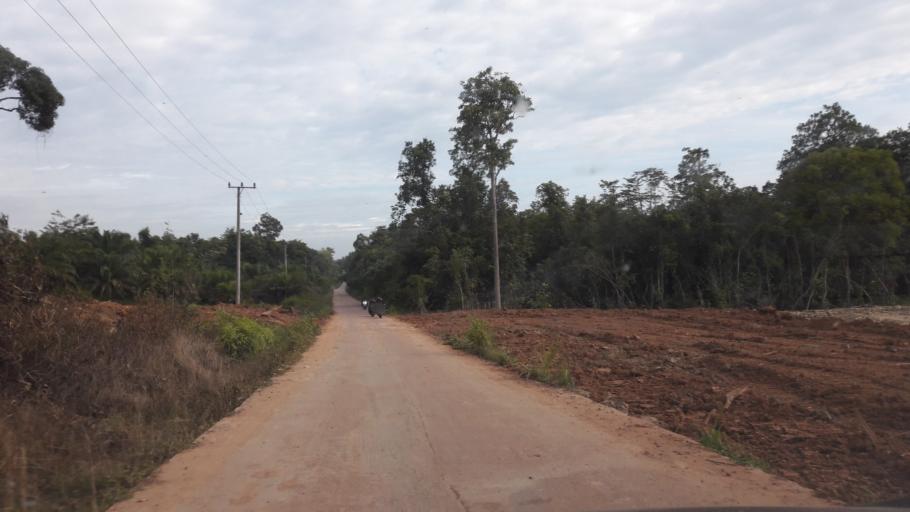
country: ID
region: South Sumatra
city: Gunungmenang
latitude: -3.2025
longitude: 103.8928
